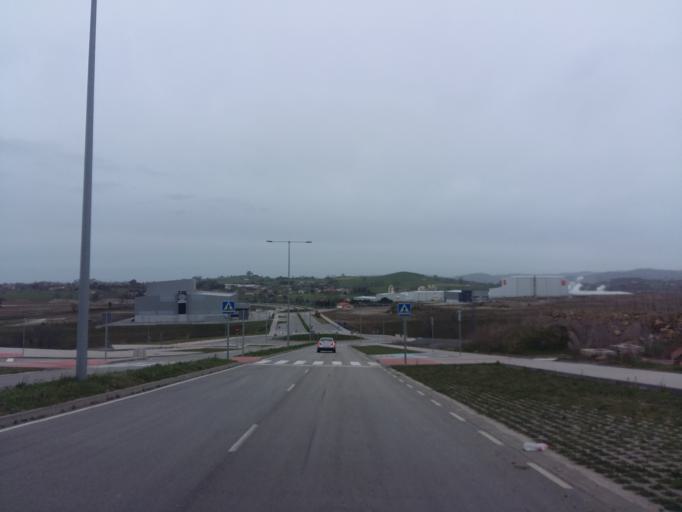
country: ES
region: Cantabria
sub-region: Provincia de Cantabria
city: Lierganes
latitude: 43.3949
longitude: -3.7465
